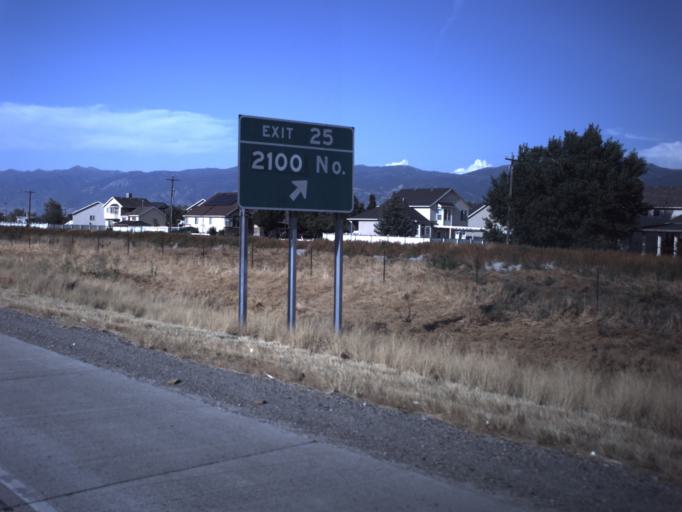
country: US
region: Utah
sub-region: Davis County
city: North Salt Lake
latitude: 40.8070
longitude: -111.9489
